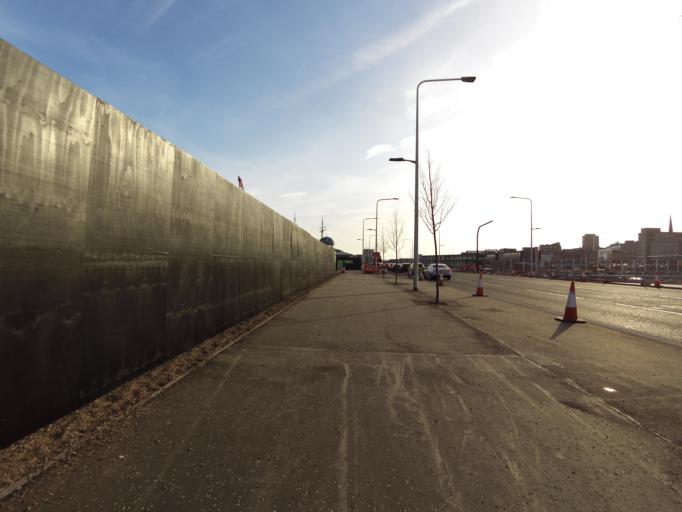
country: GB
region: Scotland
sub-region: Dundee City
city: Dundee
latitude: 56.4586
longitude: -2.9659
